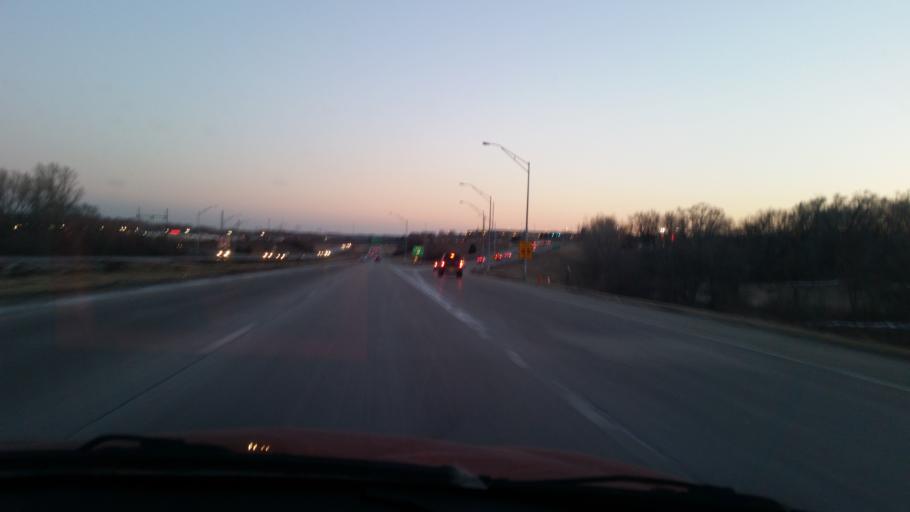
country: US
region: Nebraska
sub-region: Sarpy County
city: Offutt Air Force Base
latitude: 41.1628
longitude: -95.9391
